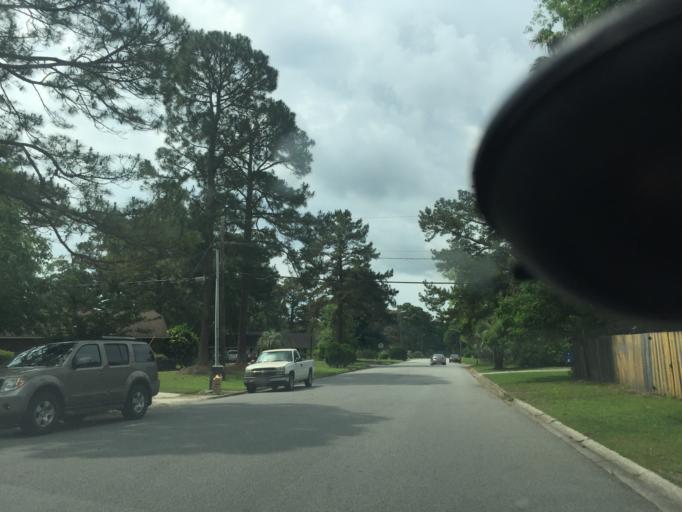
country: US
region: Georgia
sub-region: Chatham County
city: Montgomery
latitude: 32.0005
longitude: -81.1399
